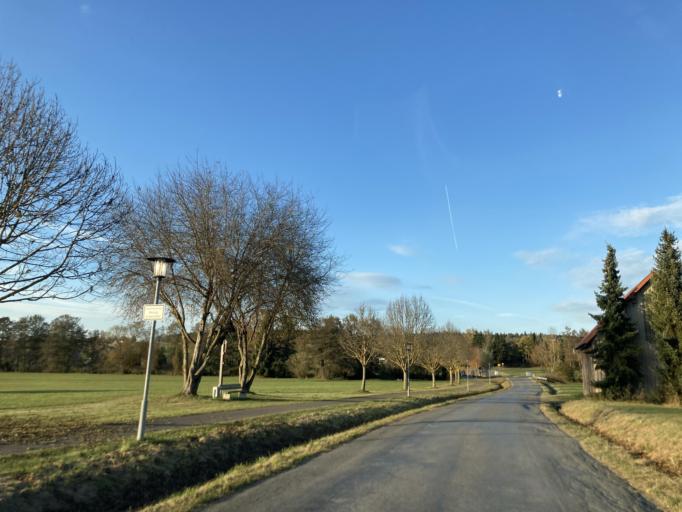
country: DE
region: Baden-Wuerttemberg
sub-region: Freiburg Region
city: Villingen-Schwenningen
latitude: 48.0271
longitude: 8.4502
